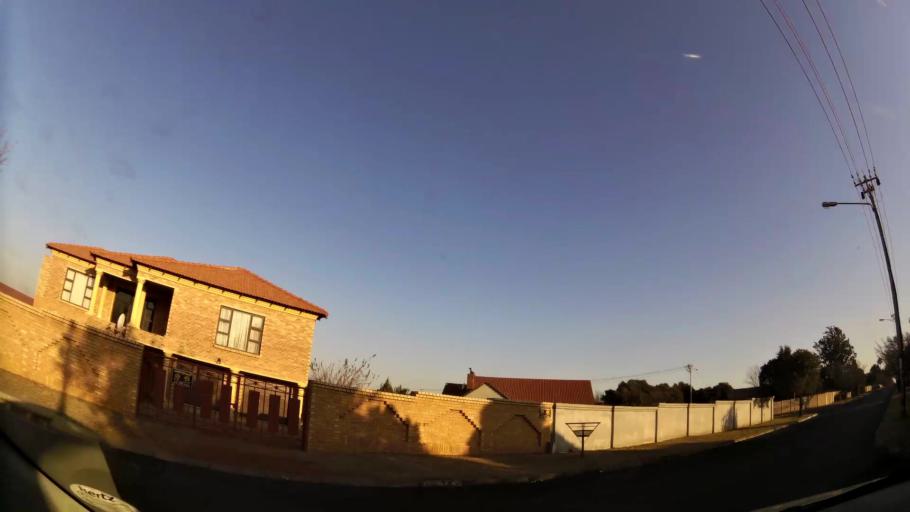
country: ZA
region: Gauteng
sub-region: West Rand District Municipality
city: Randfontein
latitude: -26.2053
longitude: 27.6590
